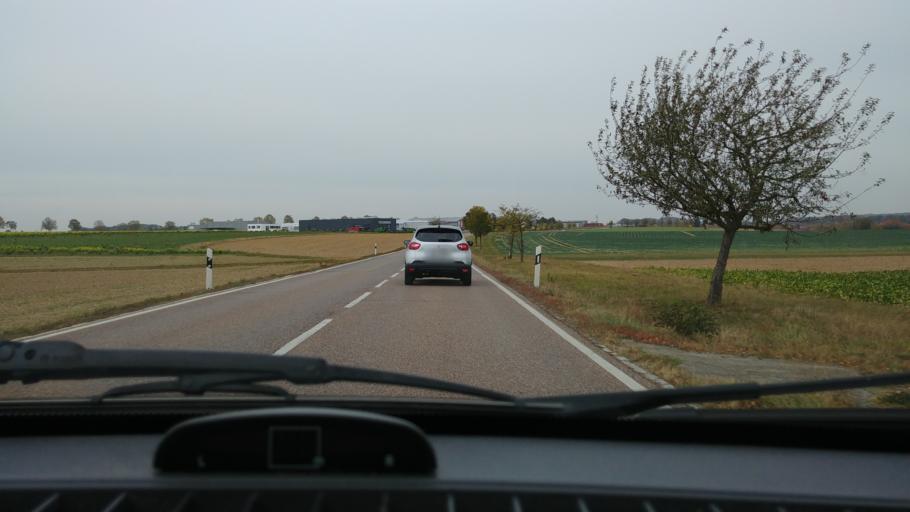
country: DE
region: Baden-Wuerttemberg
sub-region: Regierungsbezirk Stuttgart
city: Rot am See
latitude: 49.2380
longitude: 10.0374
